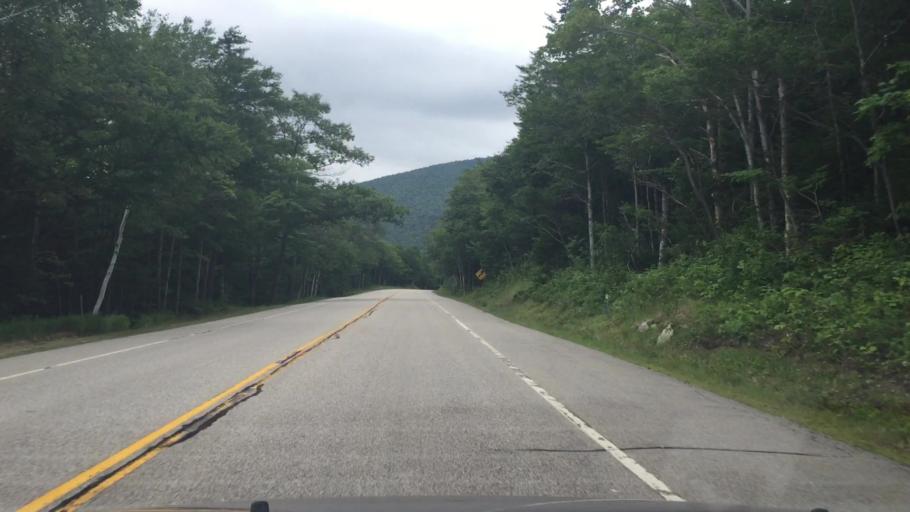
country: US
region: New Hampshire
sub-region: Grafton County
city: Deerfield
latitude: 44.1787
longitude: -71.3962
